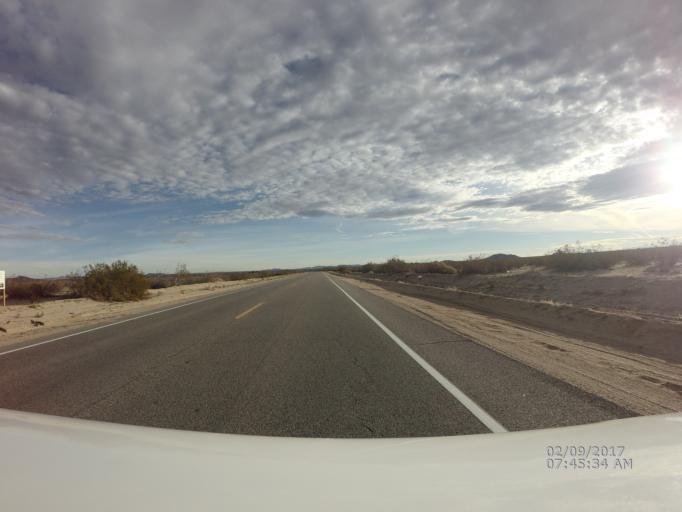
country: US
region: California
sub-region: Los Angeles County
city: Lake Los Angeles
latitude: 34.5473
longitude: -117.8330
